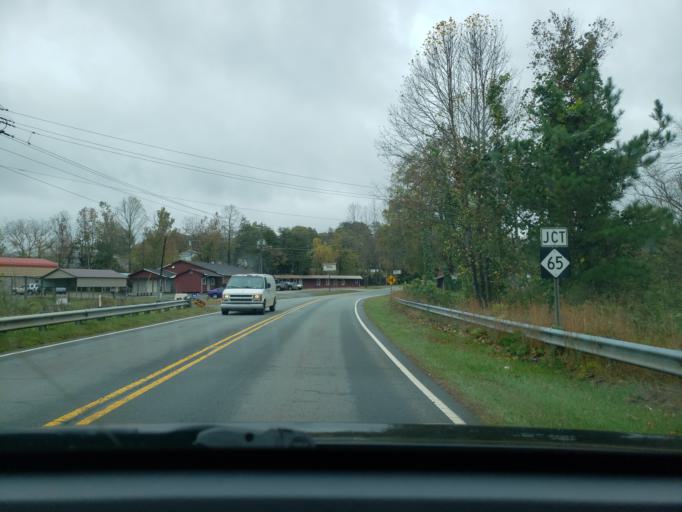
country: US
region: North Carolina
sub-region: Stokes County
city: Walnut Cove
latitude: 36.2909
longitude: -80.1408
